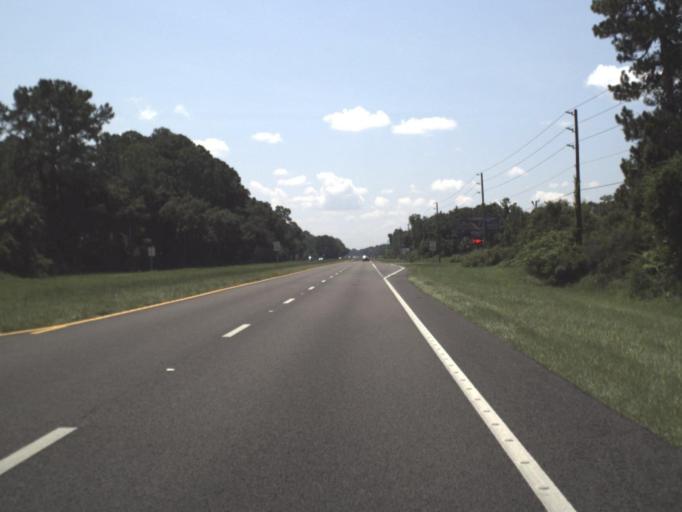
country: US
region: Florida
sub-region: Citrus County
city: Crystal River
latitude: 28.9280
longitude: -82.6147
